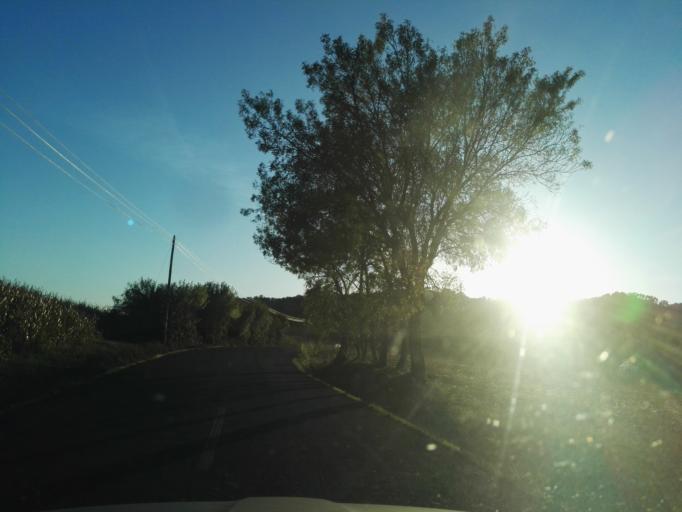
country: PT
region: Santarem
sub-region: Alpiarca
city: Alpiarca
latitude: 39.3354
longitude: -8.5872
